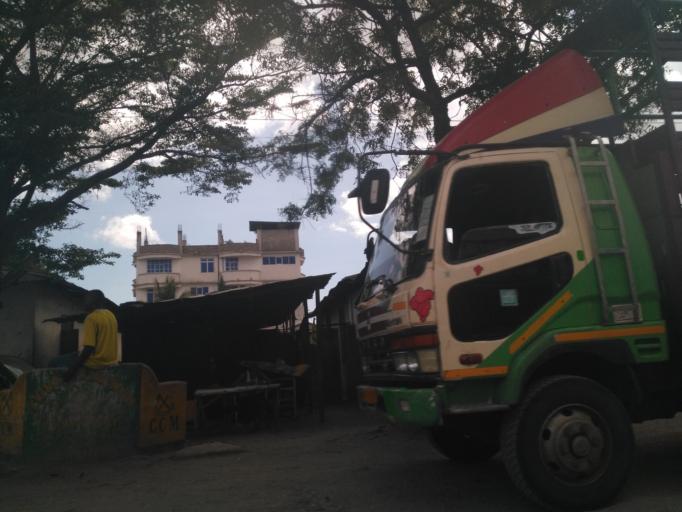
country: TZ
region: Dar es Salaam
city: Dar es Salaam
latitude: -6.8283
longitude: 39.2619
